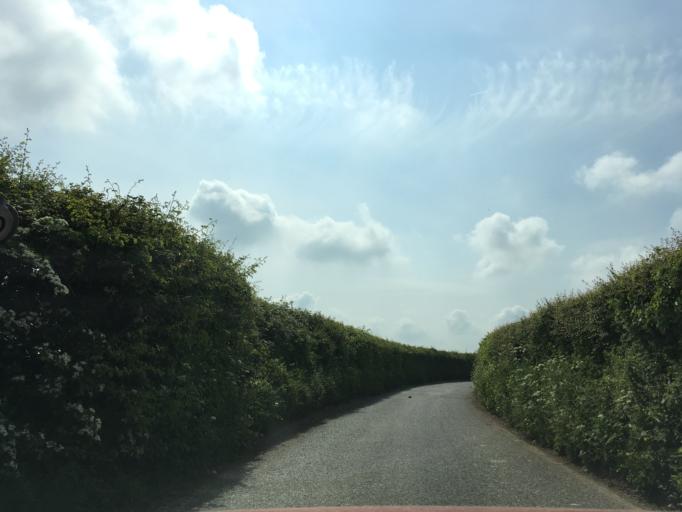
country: GB
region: England
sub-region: North Somerset
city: Dundry
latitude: 51.3979
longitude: -2.6347
